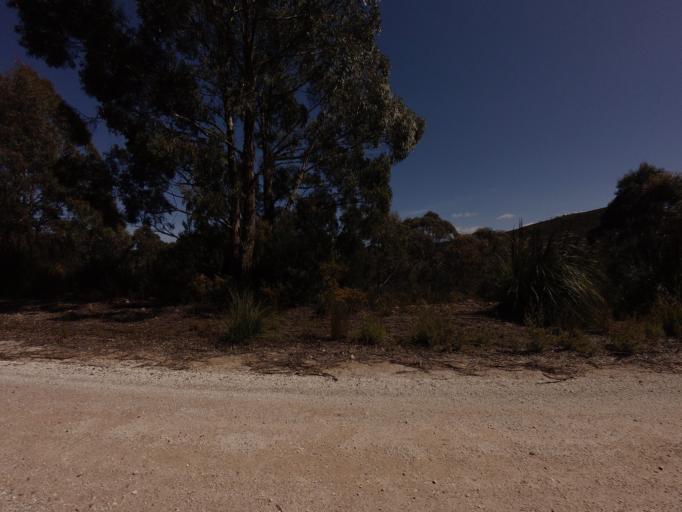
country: AU
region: Tasmania
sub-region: Huon Valley
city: Geeveston
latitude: -42.9097
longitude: 146.3634
